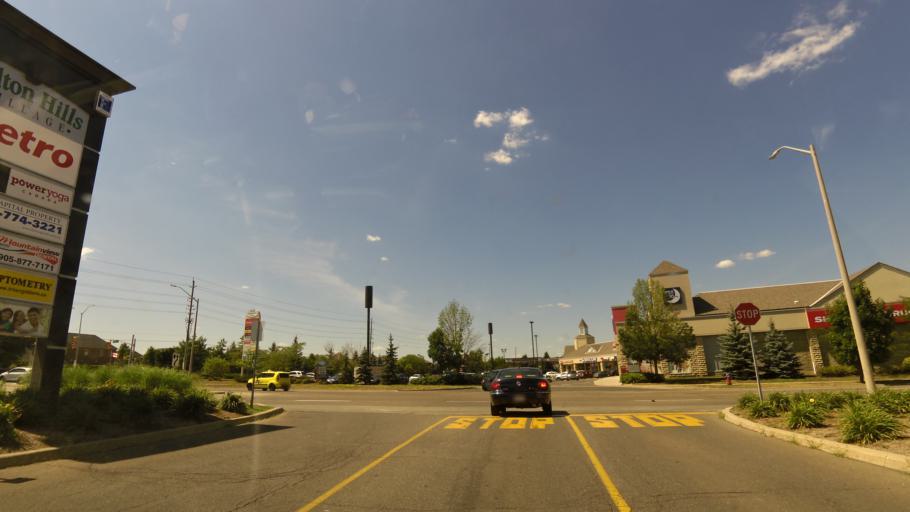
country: CA
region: Ontario
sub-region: Halton
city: Milton
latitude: 43.6323
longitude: -79.8777
